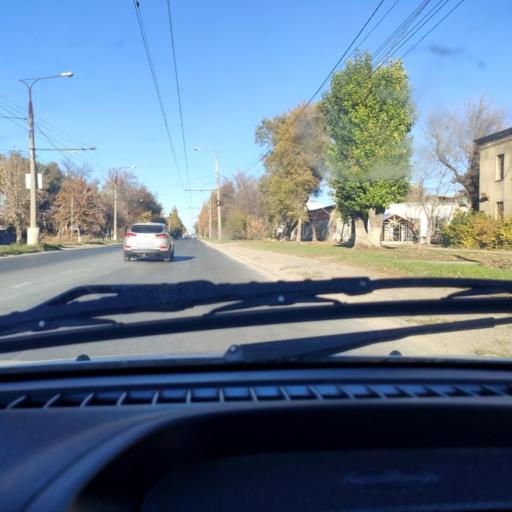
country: RU
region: Samara
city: Tol'yatti
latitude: 53.5632
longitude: 49.4555
